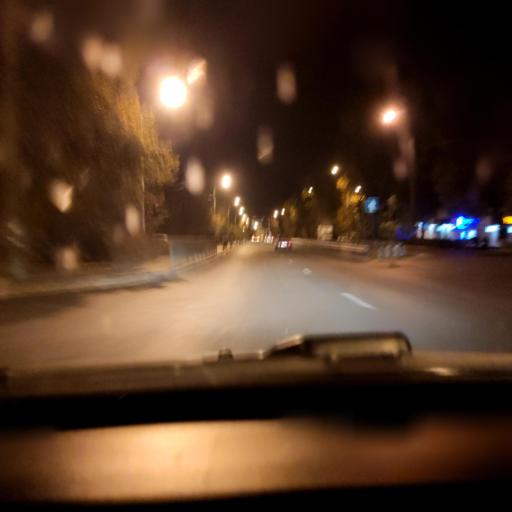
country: RU
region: Voronezj
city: Voronezh
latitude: 51.7043
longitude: 39.2294
